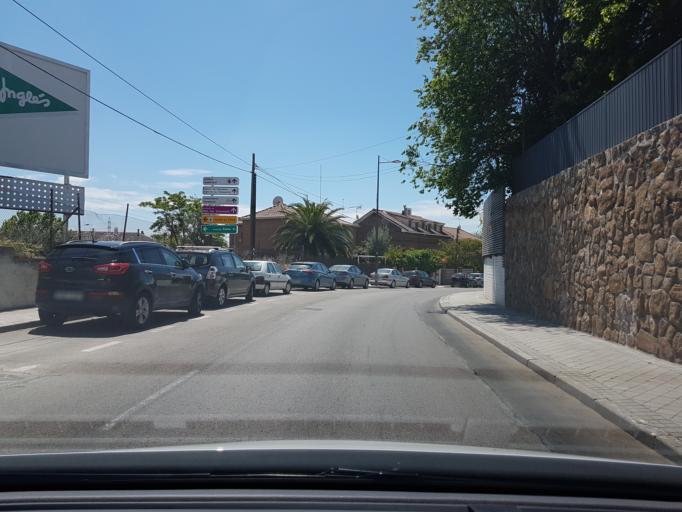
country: ES
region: Madrid
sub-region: Provincia de Madrid
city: Pozuelo de Alarcon
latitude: 40.4326
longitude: -3.8114
